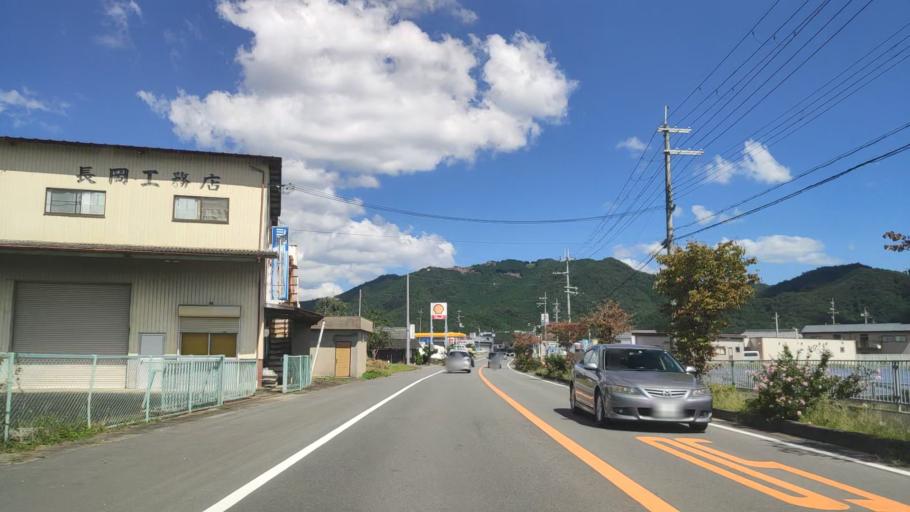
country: JP
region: Kyoto
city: Fukuchiyama
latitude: 35.2059
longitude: 135.1313
